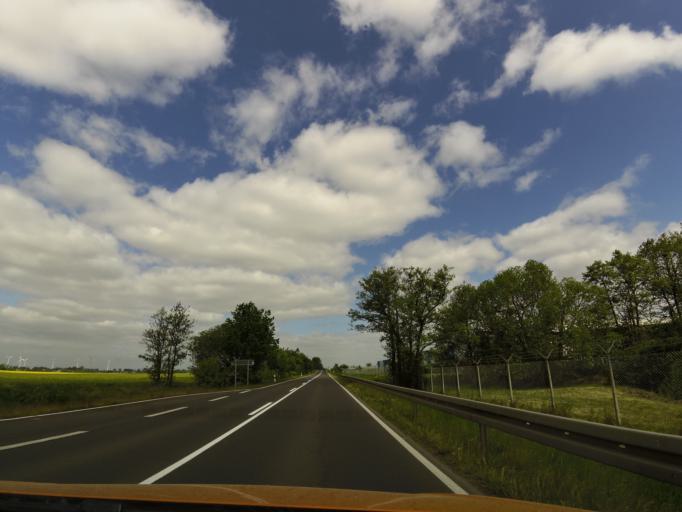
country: DE
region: Saxony-Anhalt
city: Mockern
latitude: 52.1581
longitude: 11.9425
